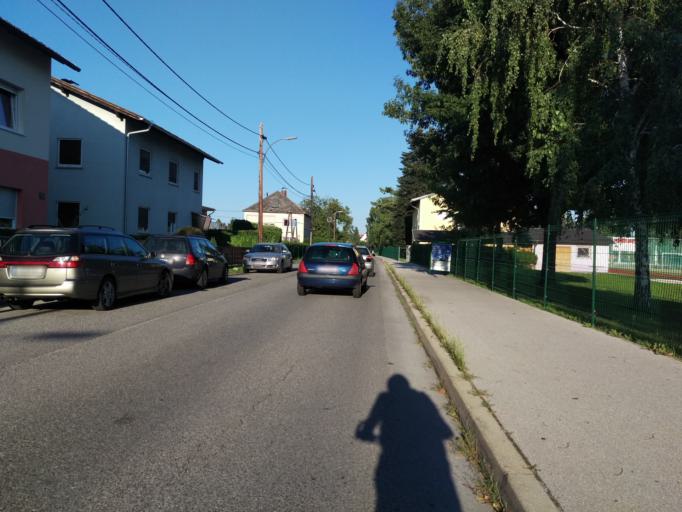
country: AT
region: Styria
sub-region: Graz Stadt
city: Wetzelsdorf
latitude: 47.0462
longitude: 15.4089
